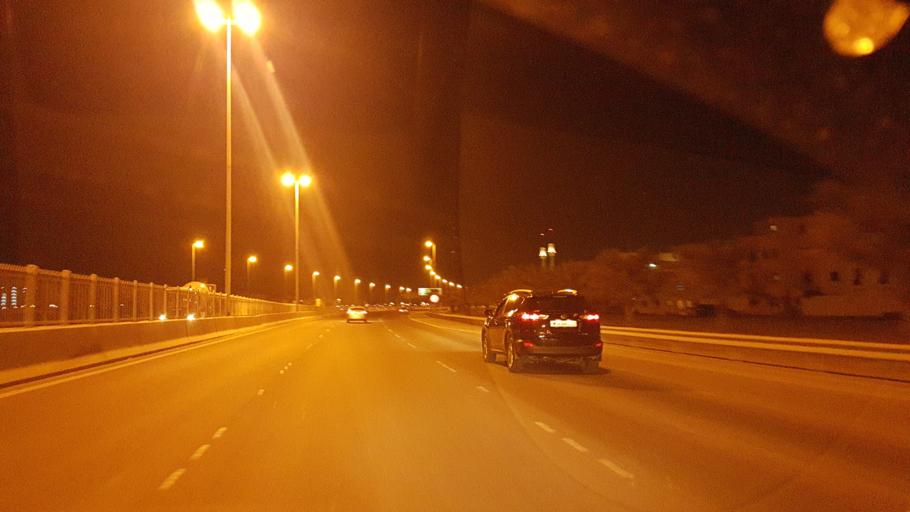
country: BH
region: Muharraq
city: Al Hadd
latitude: 26.2745
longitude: 50.6599
